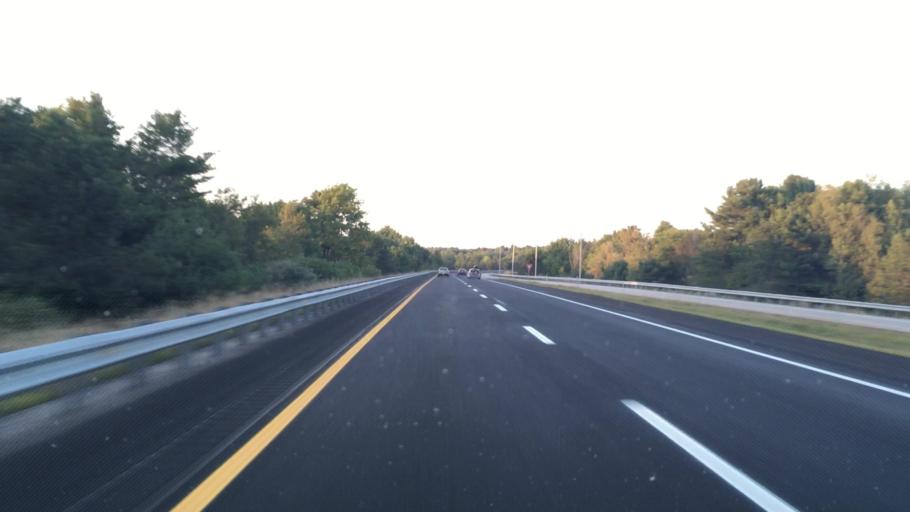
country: US
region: Maine
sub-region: Sagadahoc County
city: Topsham
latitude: 44.0195
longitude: -69.9188
